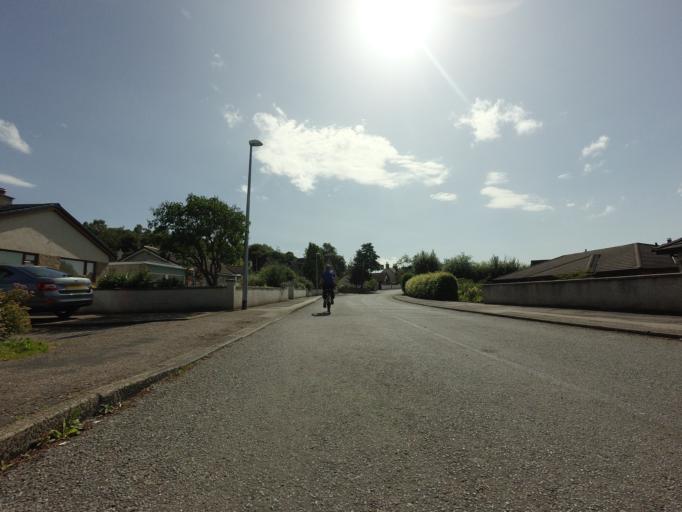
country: GB
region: Scotland
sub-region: Highland
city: Fortrose
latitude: 57.4962
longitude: -4.1213
